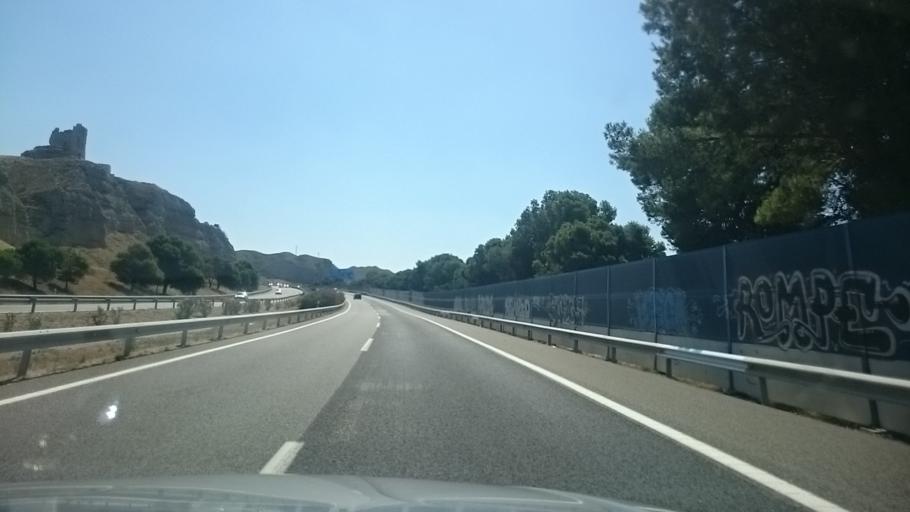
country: ES
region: Aragon
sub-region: Provincia de Zaragoza
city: Alfajarin
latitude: 41.6185
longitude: -0.7087
